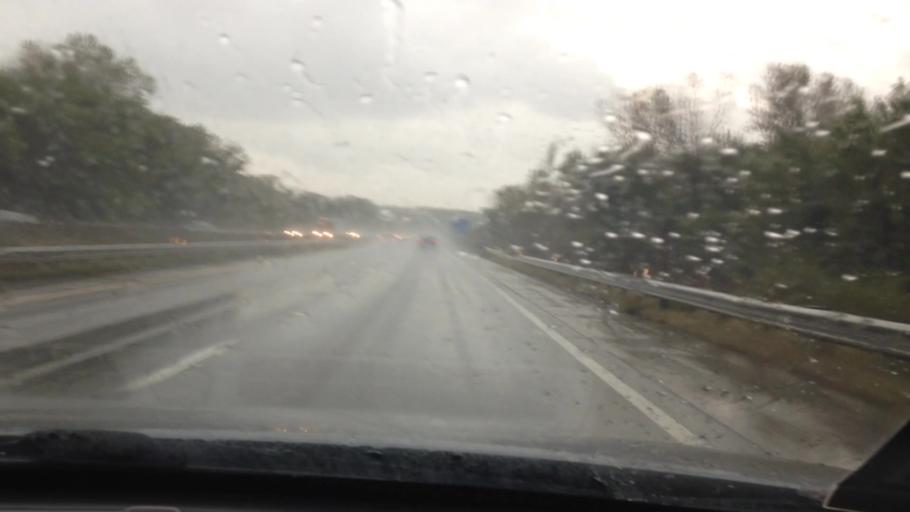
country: US
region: Missouri
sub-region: Platte County
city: Platte City
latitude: 39.3804
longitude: -94.7854
